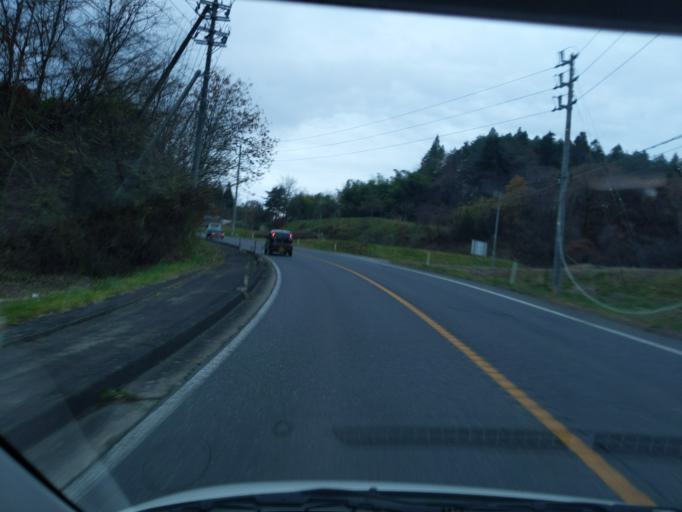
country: JP
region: Iwate
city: Ichinoseki
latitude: 39.0139
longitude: 141.3283
